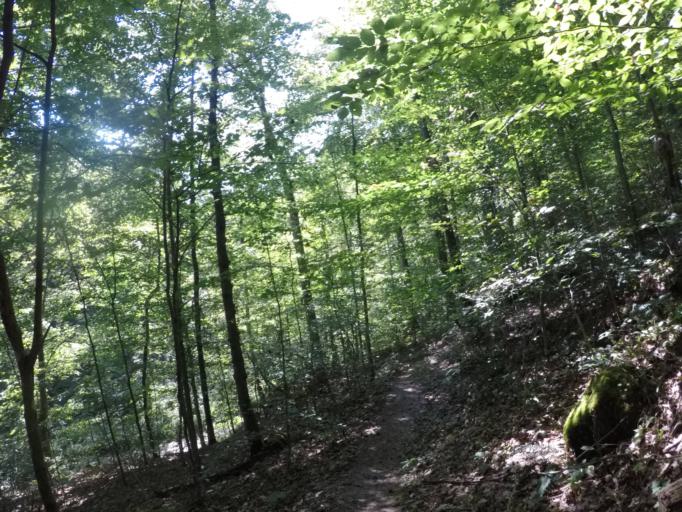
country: US
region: Ohio
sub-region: Lawrence County
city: Ironton
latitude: 38.6254
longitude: -82.6152
